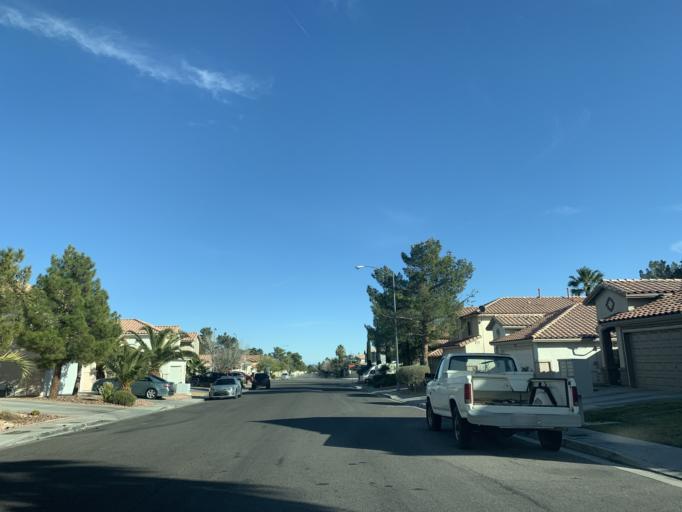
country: US
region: Nevada
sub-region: Clark County
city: Summerlin South
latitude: 36.1280
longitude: -115.3074
